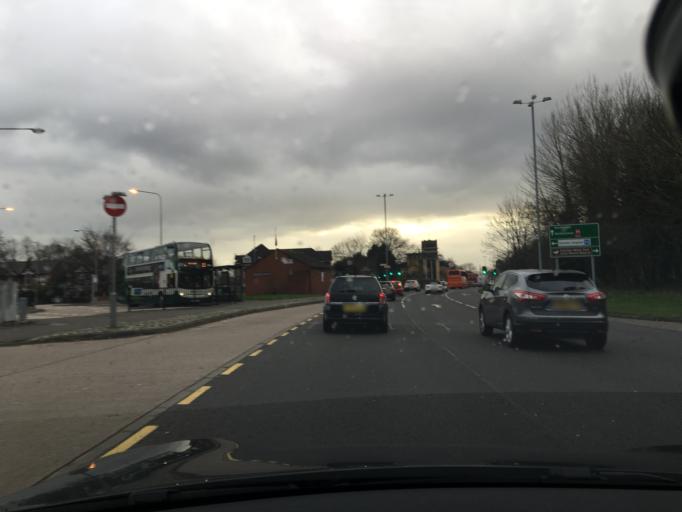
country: GB
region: England
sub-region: Manchester
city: Chorlton cum Hardy
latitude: 53.4258
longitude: -2.2541
